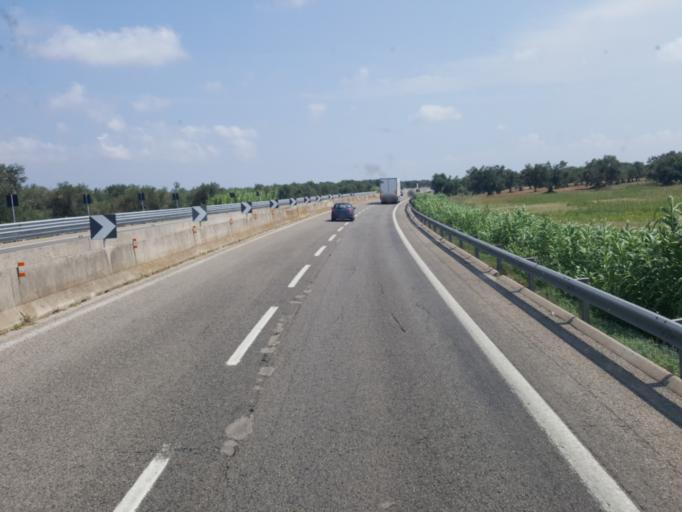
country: IT
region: Apulia
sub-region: Provincia di Brindisi
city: Torchiarolo
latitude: 40.5005
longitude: 18.0314
